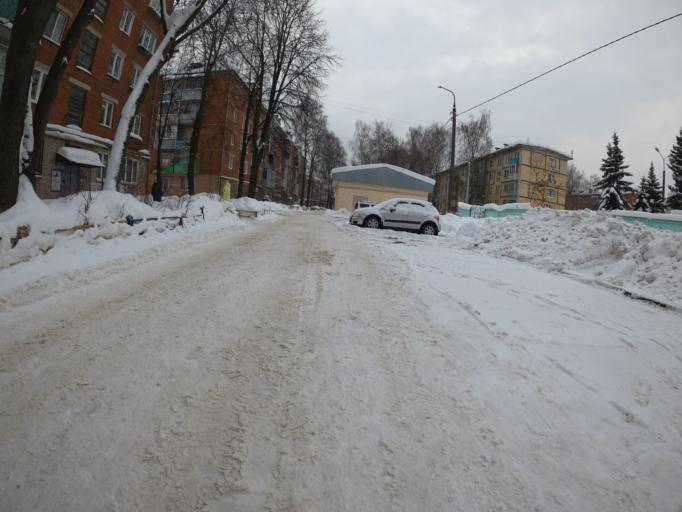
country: RU
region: Moskovskaya
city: Elektrogorsk
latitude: 55.8760
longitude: 38.7864
